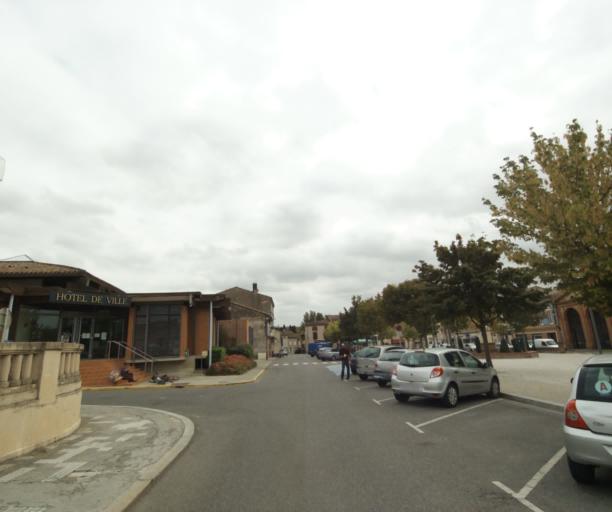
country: FR
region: Midi-Pyrenees
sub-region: Departement de la Haute-Garonne
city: Villefranche-de-Lauragais
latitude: 43.3992
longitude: 1.7183
